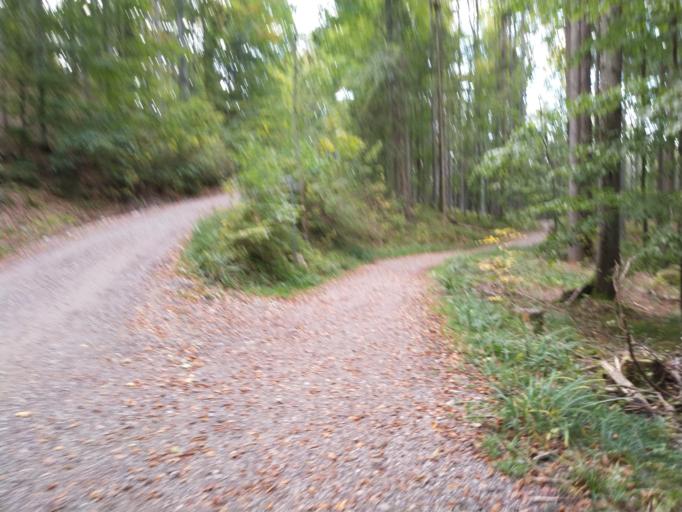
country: AT
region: Tyrol
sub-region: Politischer Bezirk Reutte
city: Vils
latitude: 47.5652
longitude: 10.6394
